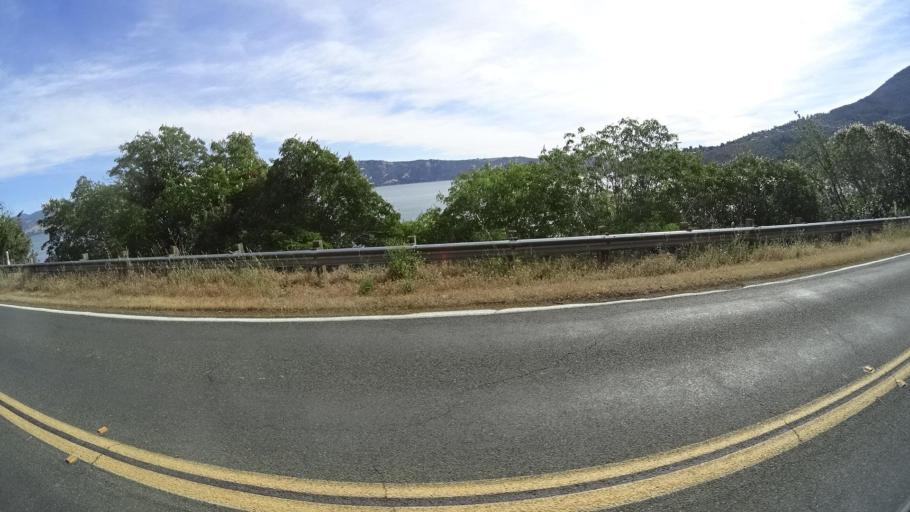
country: US
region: California
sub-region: Lake County
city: Soda Bay
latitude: 39.0081
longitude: -122.8017
